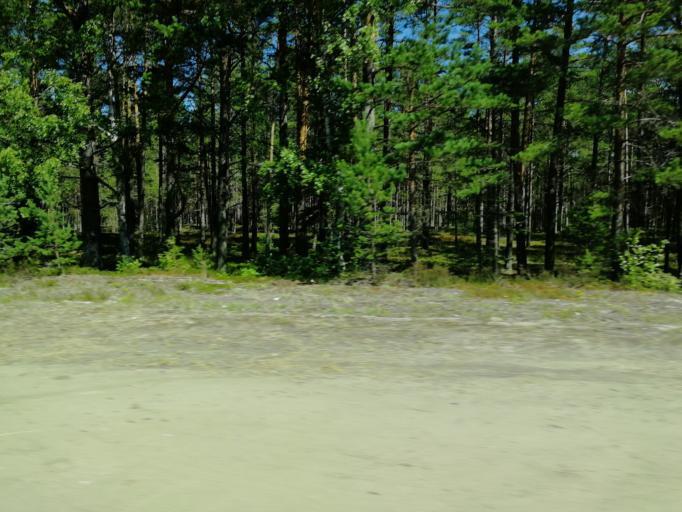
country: LV
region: Rojas
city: Roja
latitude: 57.5091
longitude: 22.7929
